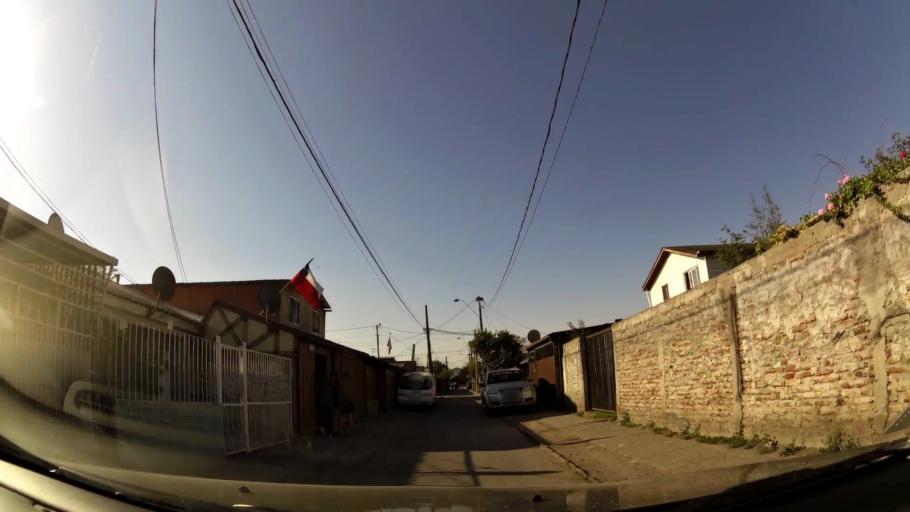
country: CL
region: Santiago Metropolitan
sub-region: Provincia de Santiago
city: La Pintana
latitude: -33.5813
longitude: -70.6607
